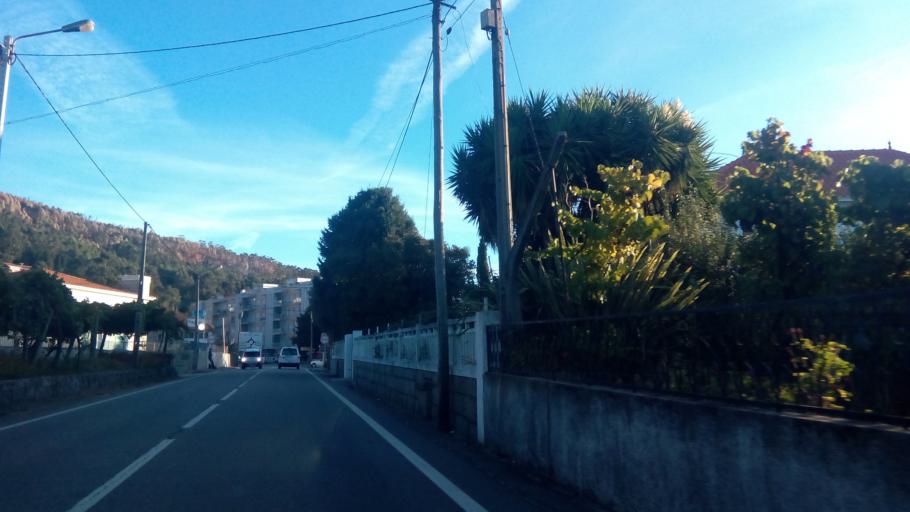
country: PT
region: Porto
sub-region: Paredes
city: Baltar
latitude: 41.1904
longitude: -8.3886
